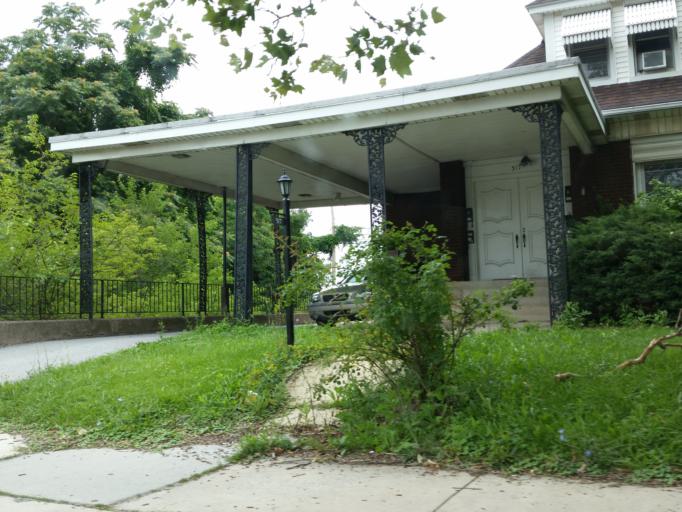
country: US
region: Pennsylvania
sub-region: York County
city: North York
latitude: 39.9706
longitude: -76.7317
